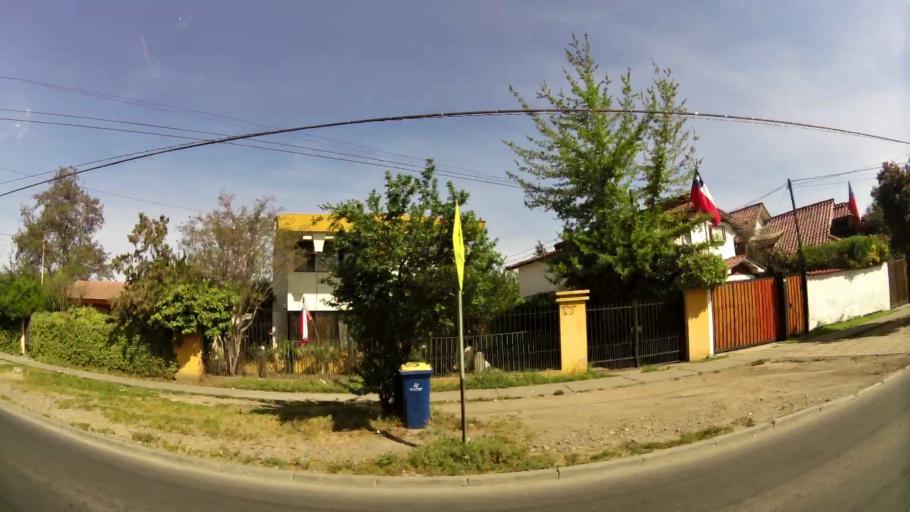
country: CL
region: Santiago Metropolitan
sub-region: Provincia de Santiago
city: La Pintana
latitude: -33.5361
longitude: -70.5801
